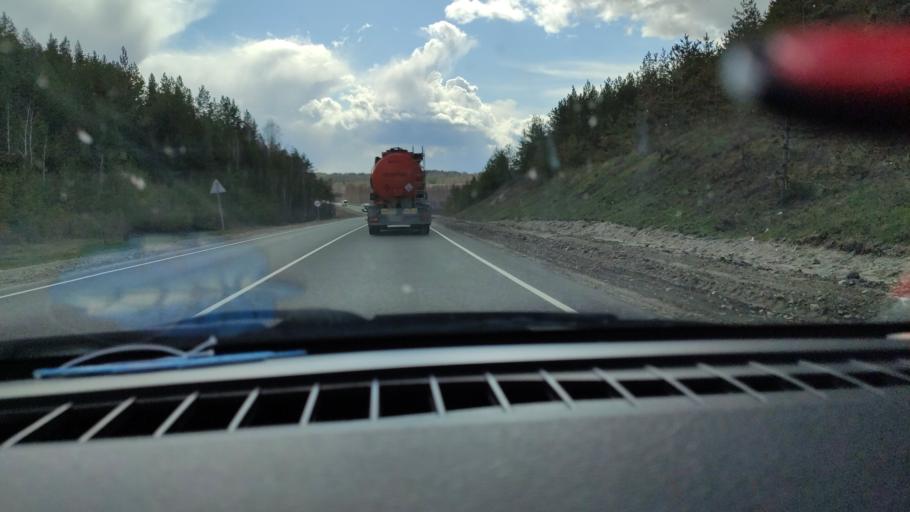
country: RU
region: Saratov
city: Khvalynsk
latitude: 52.5291
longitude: 48.0276
